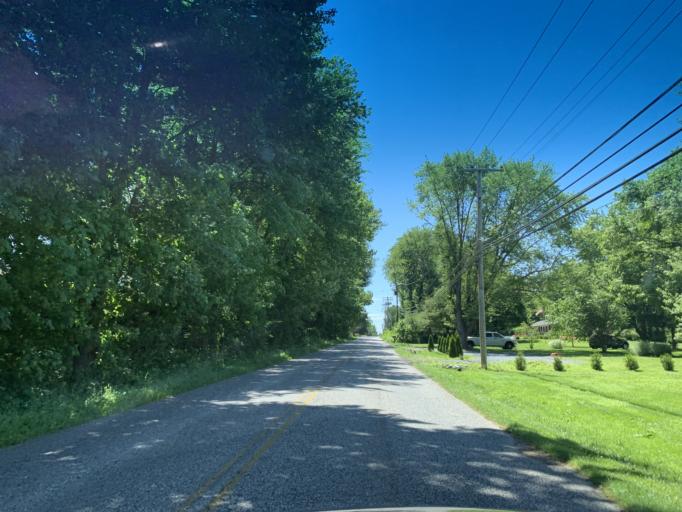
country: US
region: Maryland
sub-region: Harford County
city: Havre de Grace
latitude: 39.5548
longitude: -76.1367
